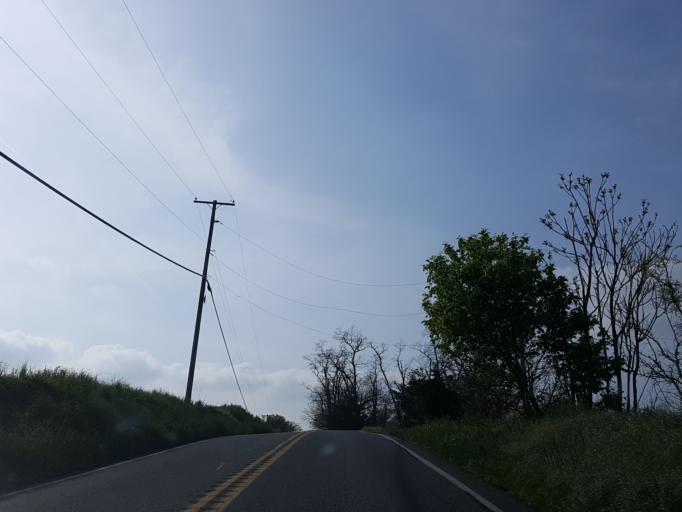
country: US
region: Pennsylvania
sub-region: Lebanon County
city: Campbelltown
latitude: 40.2389
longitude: -76.5885
